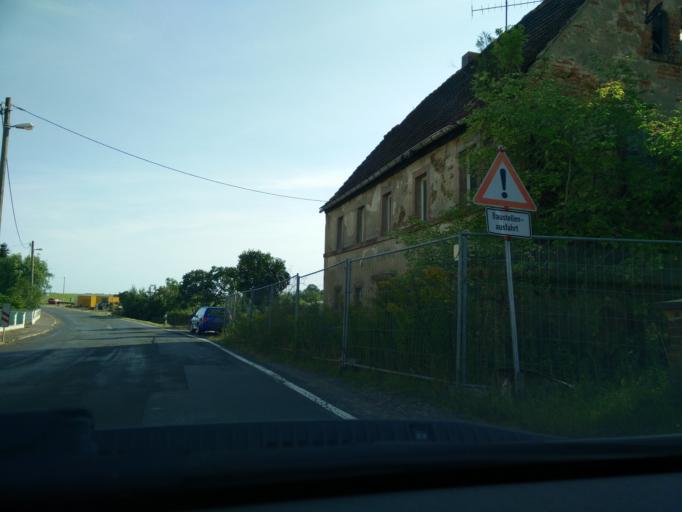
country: DE
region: Saxony
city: Otterwisch
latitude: 51.1737
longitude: 12.6211
